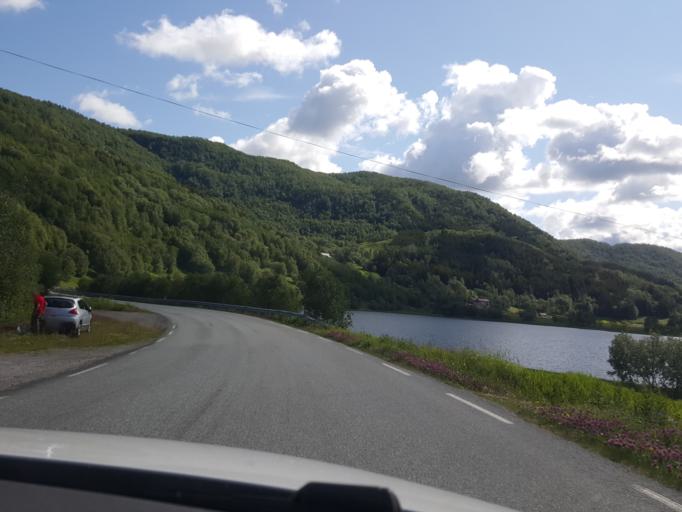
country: NO
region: Nordland
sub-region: Bodo
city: Loding
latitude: 67.0863
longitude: 14.9866
